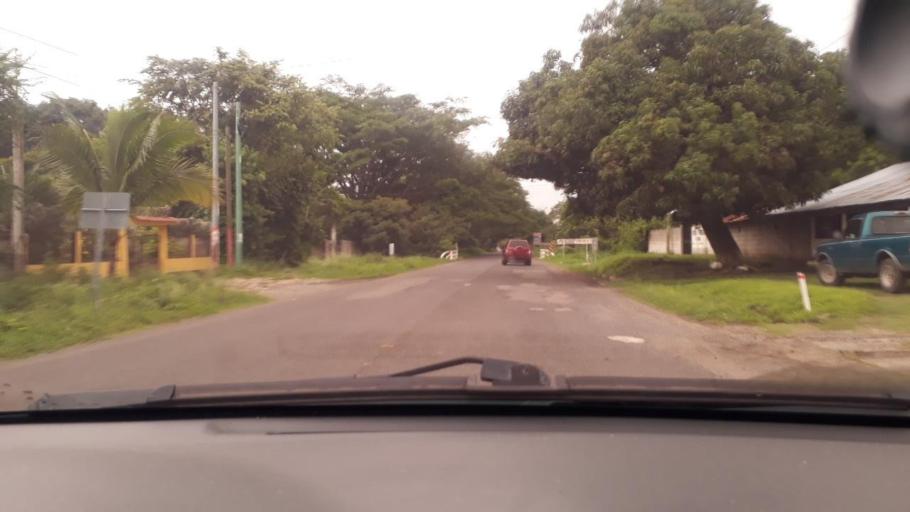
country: GT
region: Jutiapa
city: Jalpatagua
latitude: 14.1564
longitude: -90.0505
